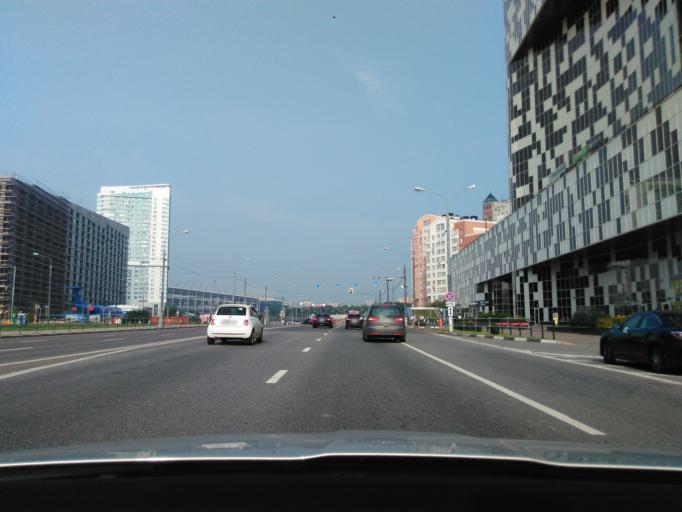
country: RU
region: Moscow
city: Sokol
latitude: 55.7919
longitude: 37.5288
